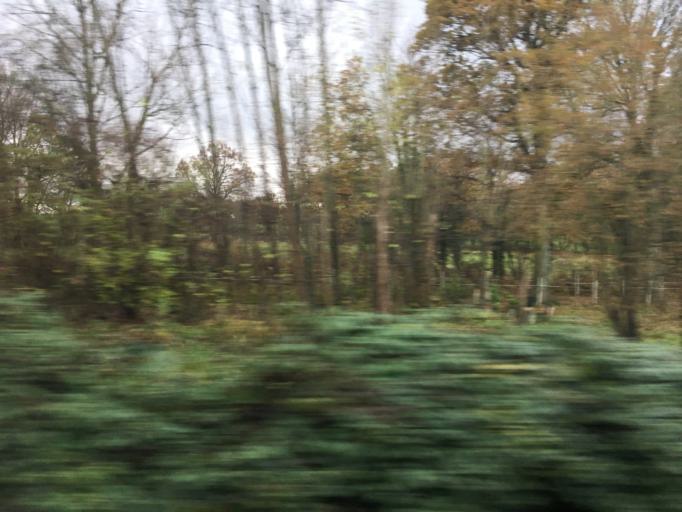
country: DE
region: North Rhine-Westphalia
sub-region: Regierungsbezirk Munster
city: Altenberge
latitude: 52.0403
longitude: 7.4955
